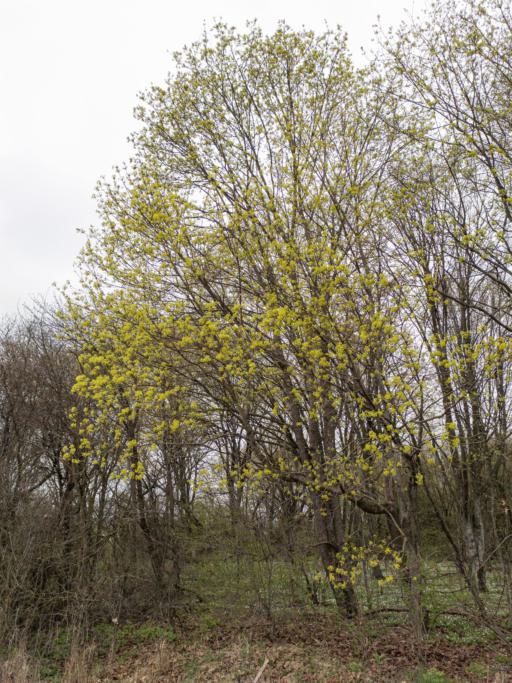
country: BY
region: Brest
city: Pruzhany
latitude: 52.4875
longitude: 24.6293
